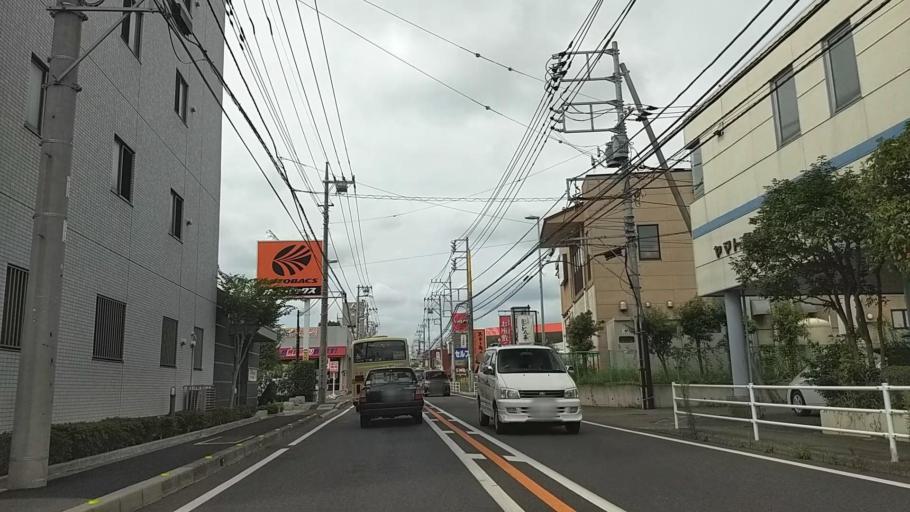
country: JP
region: Kanagawa
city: Minami-rinkan
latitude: 35.4576
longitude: 139.4671
